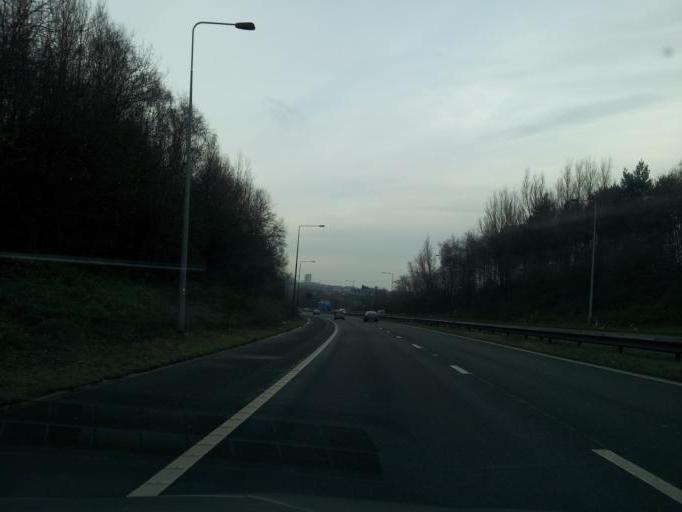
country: GB
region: England
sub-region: Borough of Oldham
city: Royton
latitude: 53.5632
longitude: -2.1528
